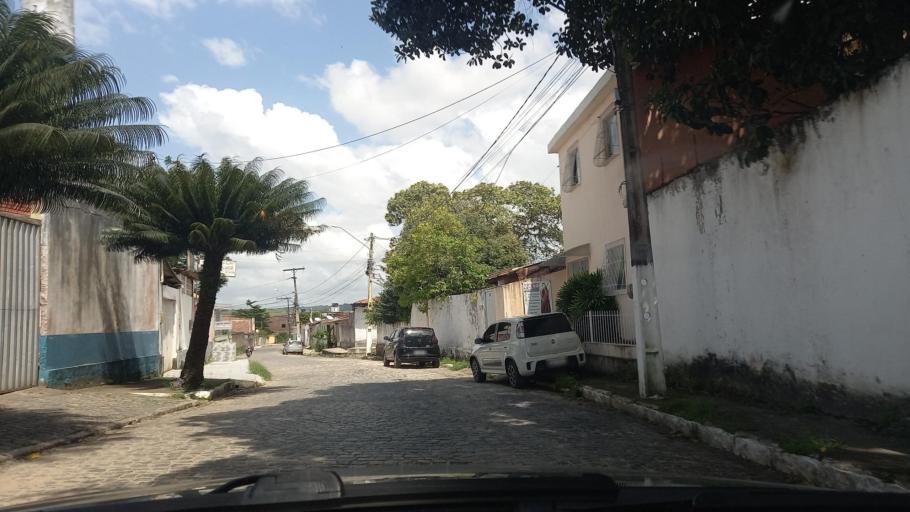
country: BR
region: Pernambuco
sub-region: Goiana
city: Goiana
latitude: -7.5644
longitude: -34.9980
